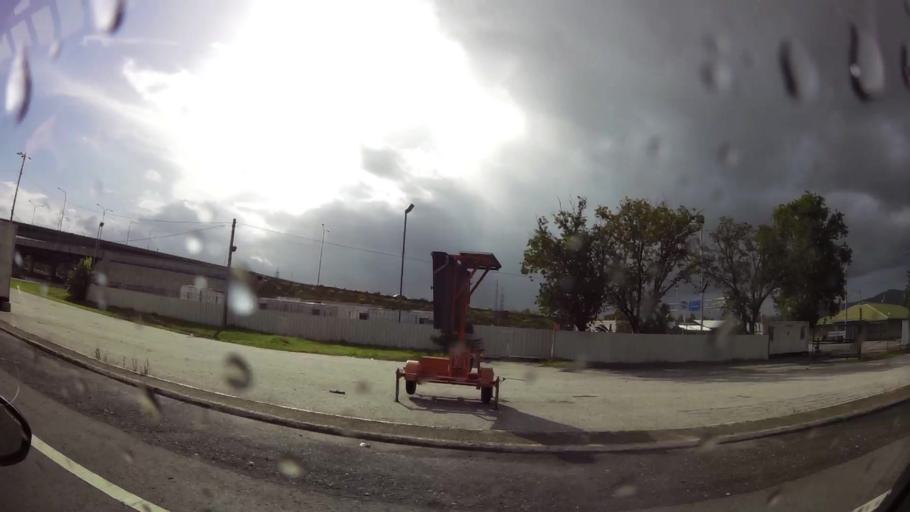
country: TT
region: Tunapuna/Piarco
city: Tunapuna
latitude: 10.6337
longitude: -61.4293
